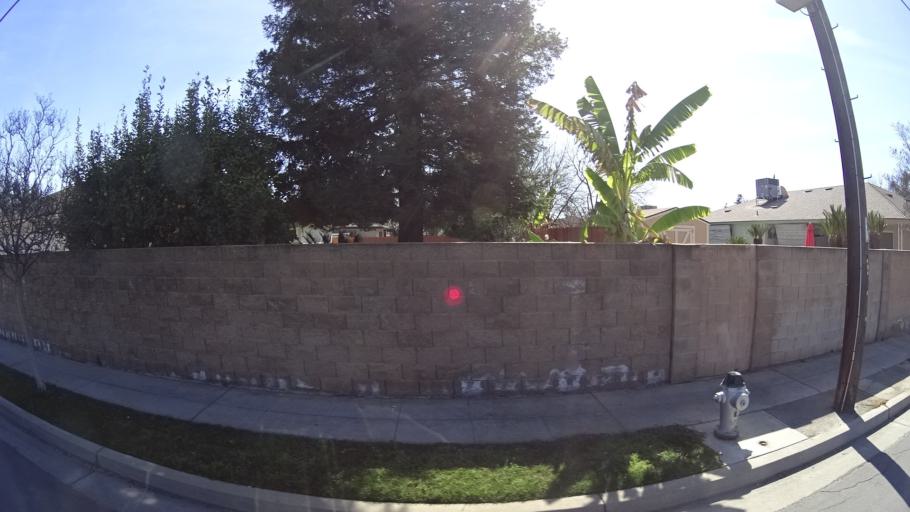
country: US
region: California
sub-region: Fresno County
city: Clovis
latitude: 36.8446
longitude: -119.7718
